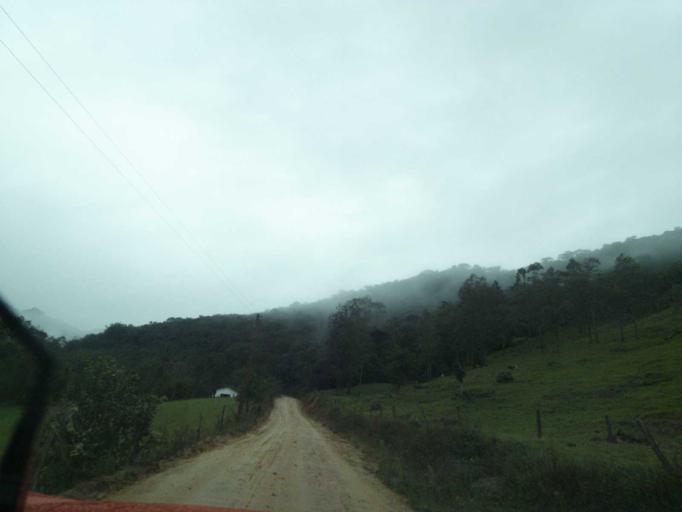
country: BR
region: Santa Catarina
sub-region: Anitapolis
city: Anitapolis
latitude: -27.9032
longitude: -49.1958
